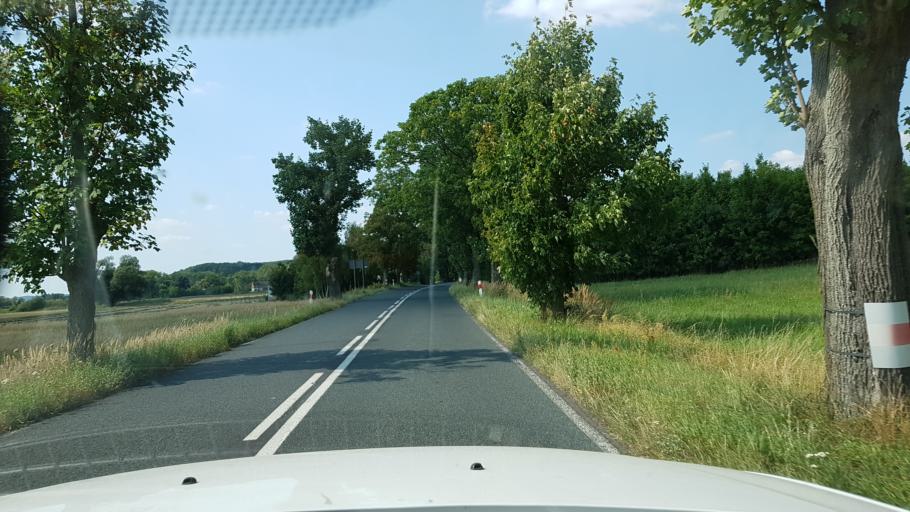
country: PL
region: West Pomeranian Voivodeship
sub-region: Powiat gryfinski
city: Cedynia
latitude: 52.8331
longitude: 14.2051
